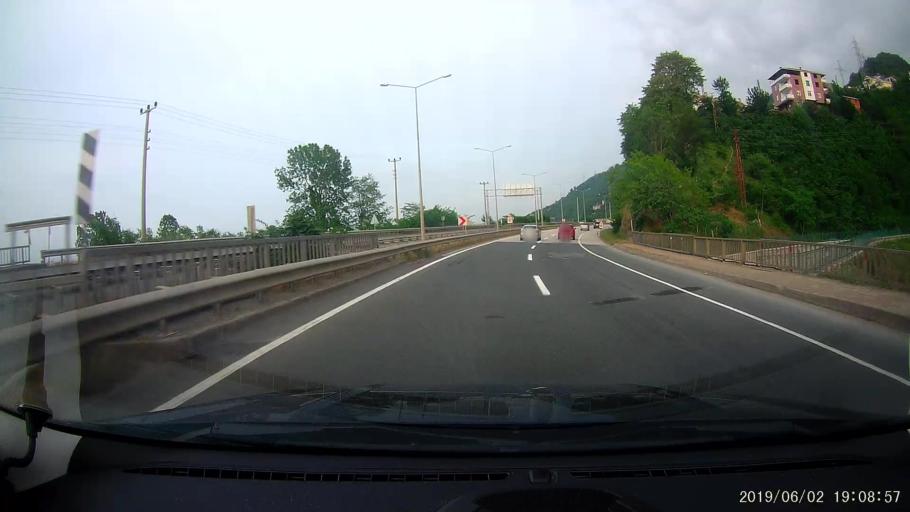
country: TR
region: Ordu
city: Gulyali
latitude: 40.9761
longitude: 38.0196
